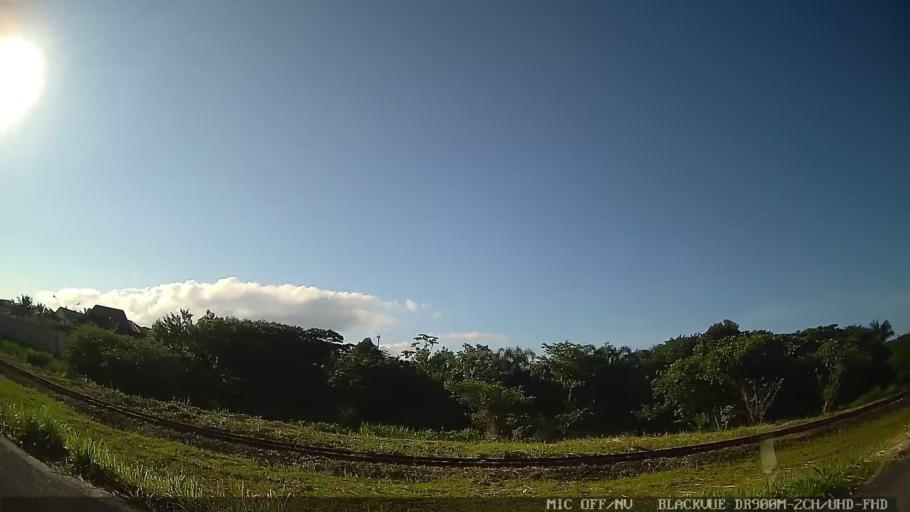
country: BR
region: Sao Paulo
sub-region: Peruibe
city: Peruibe
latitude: -24.2810
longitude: -46.9603
